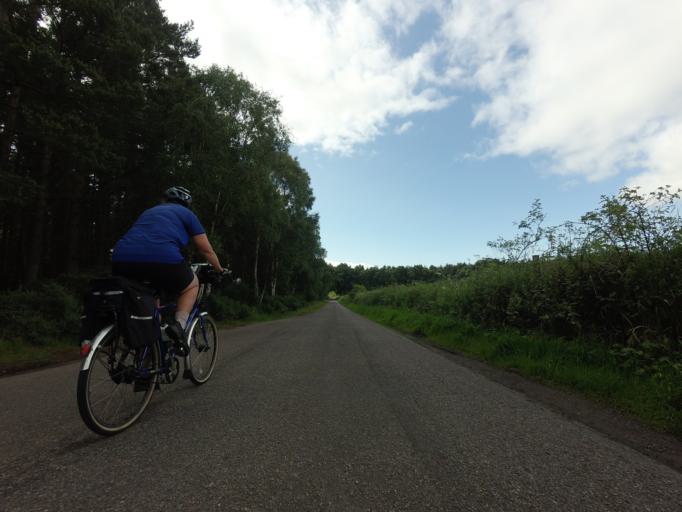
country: GB
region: Scotland
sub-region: Highland
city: Nairn
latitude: 57.5623
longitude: -3.8671
